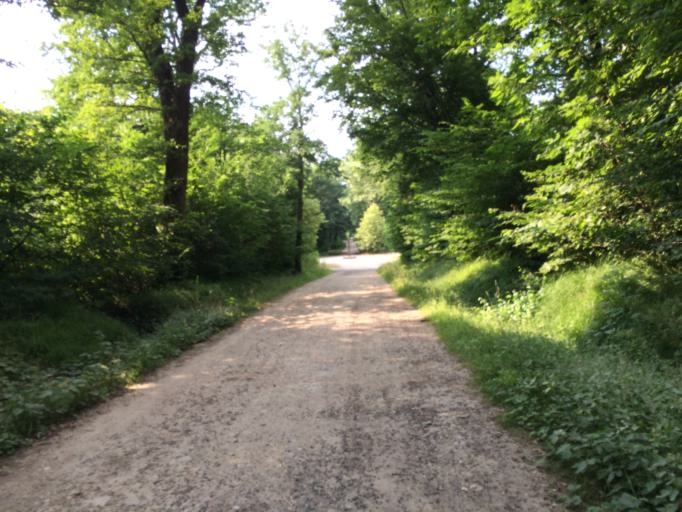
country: FR
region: Ile-de-France
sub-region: Departement de l'Essonne
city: Bievres
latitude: 48.7657
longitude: 2.2392
